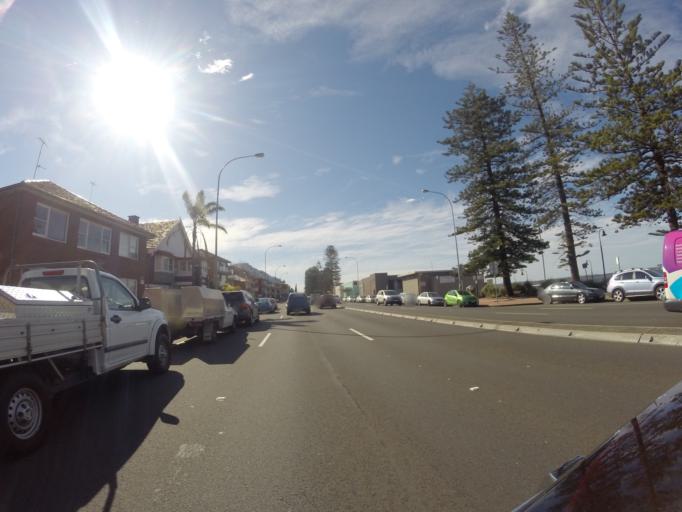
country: AU
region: New South Wales
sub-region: Rockdale
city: Brighton-Le-Sands
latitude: -33.9636
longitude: 151.1551
